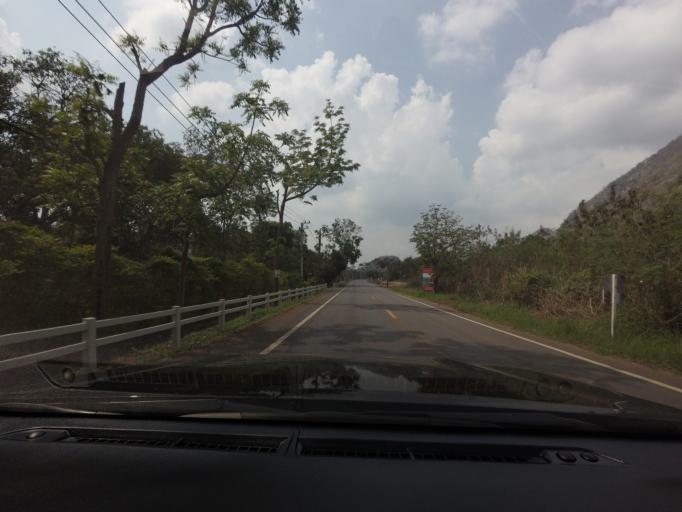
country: TH
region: Sara Buri
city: Muak Lek
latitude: 14.5828
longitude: 101.2563
